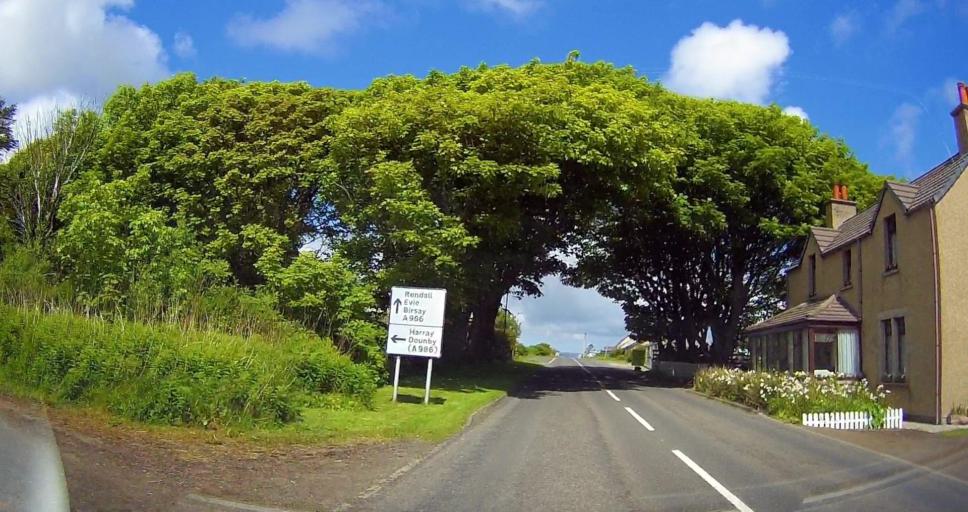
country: GB
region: Scotland
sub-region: Orkney Islands
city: Orkney
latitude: 59.0459
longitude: -3.0836
